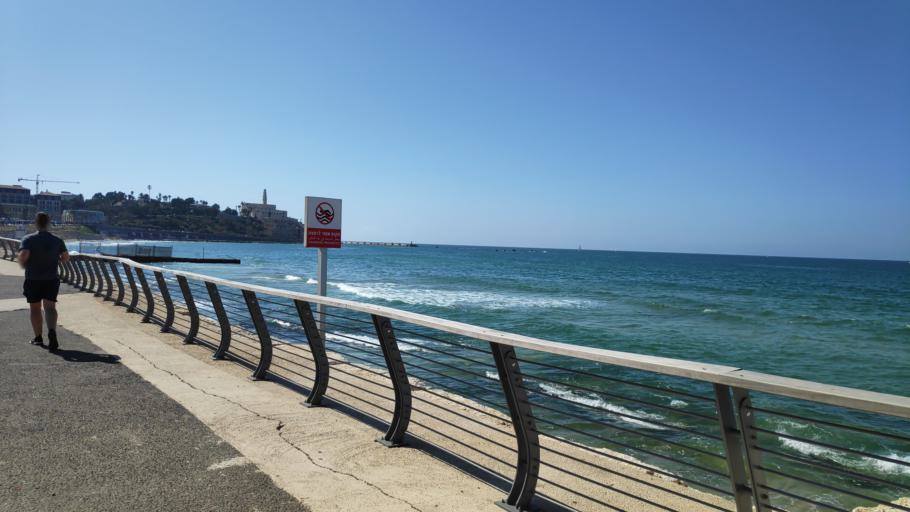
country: IL
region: Tel Aviv
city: Yafo
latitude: 32.0592
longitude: 34.7583
